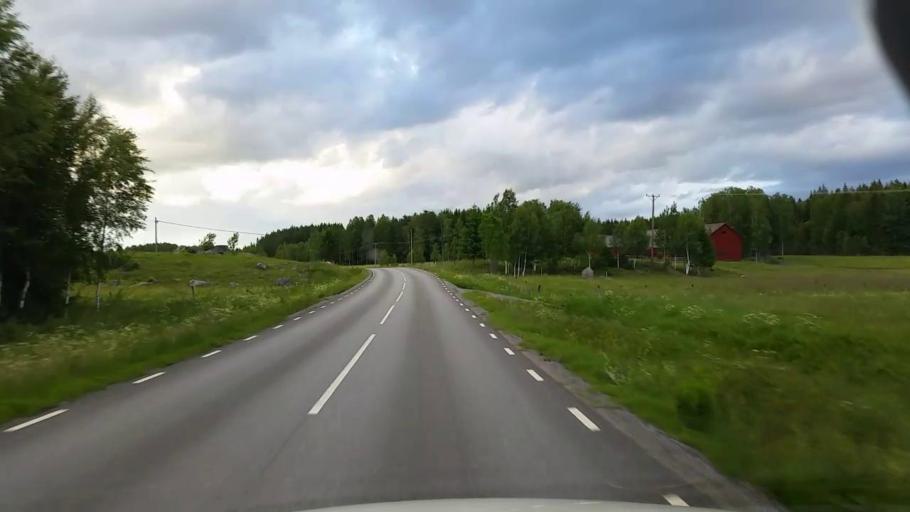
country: SE
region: Vaestmanland
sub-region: Kopings Kommun
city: Kolsva
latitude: 59.7628
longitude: 15.8444
